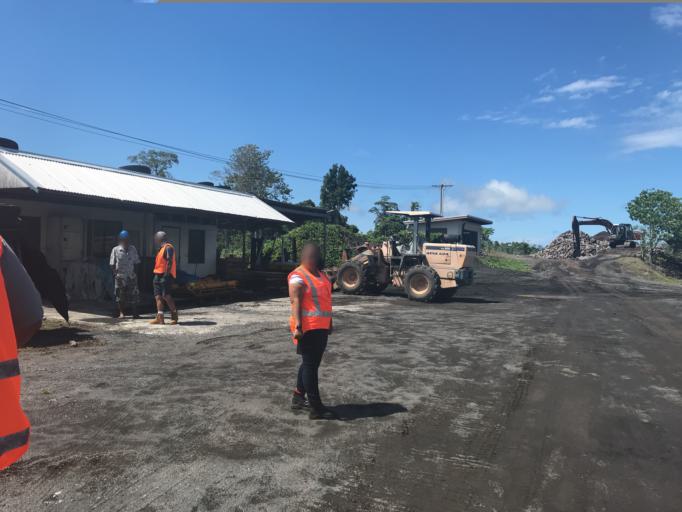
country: WS
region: Palauli
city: Vailoa
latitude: -13.7478
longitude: -172.2337
